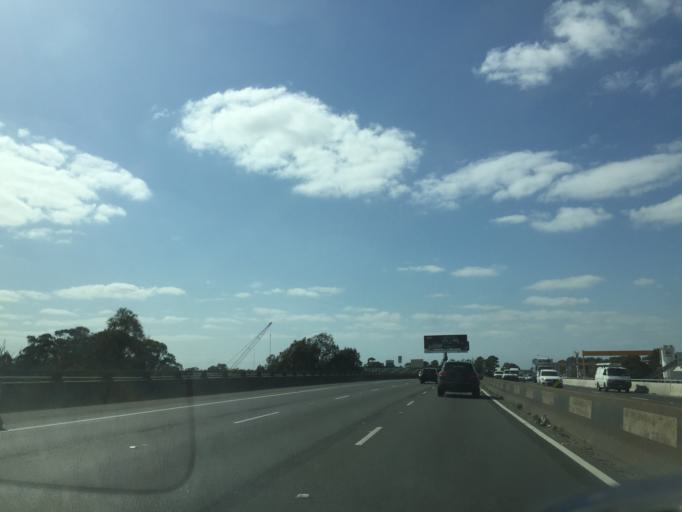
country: AU
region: New South Wales
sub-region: Parramatta
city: Granville
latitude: -33.8346
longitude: 151.0286
